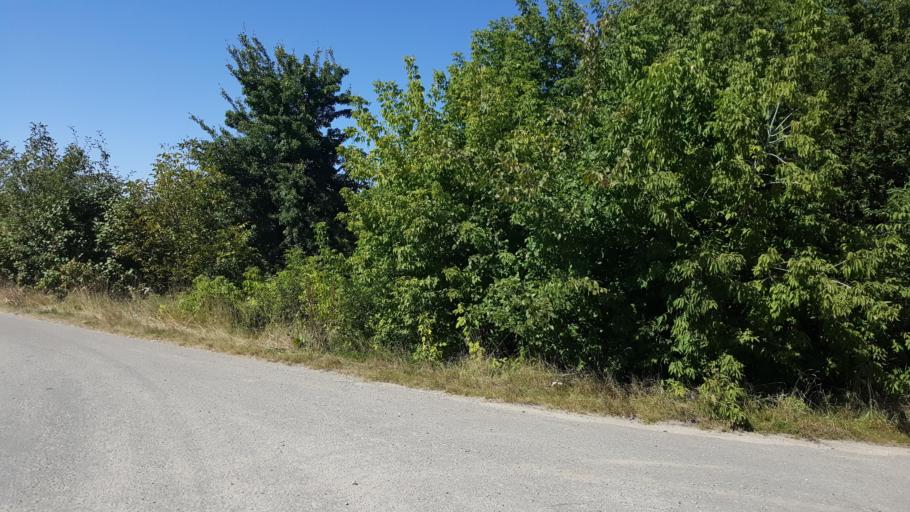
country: PL
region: Lublin Voivodeship
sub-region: Powiat bialski
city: Rokitno
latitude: 52.2313
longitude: 23.3453
